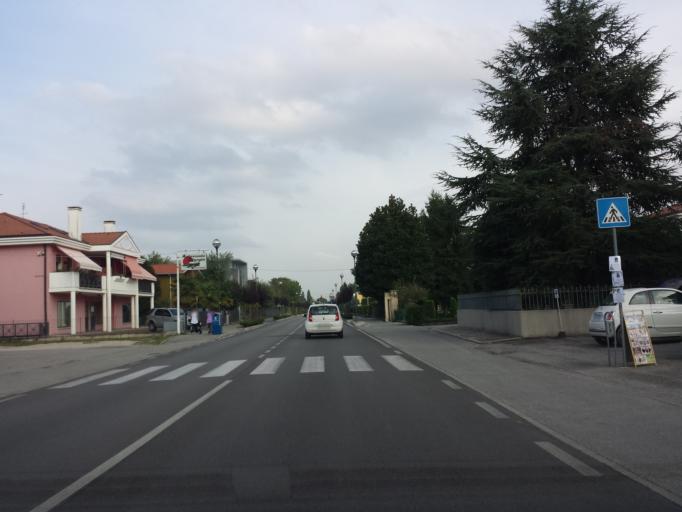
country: IT
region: Veneto
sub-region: Provincia di Padova
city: Campodarsego
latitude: 45.5008
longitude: 11.9126
